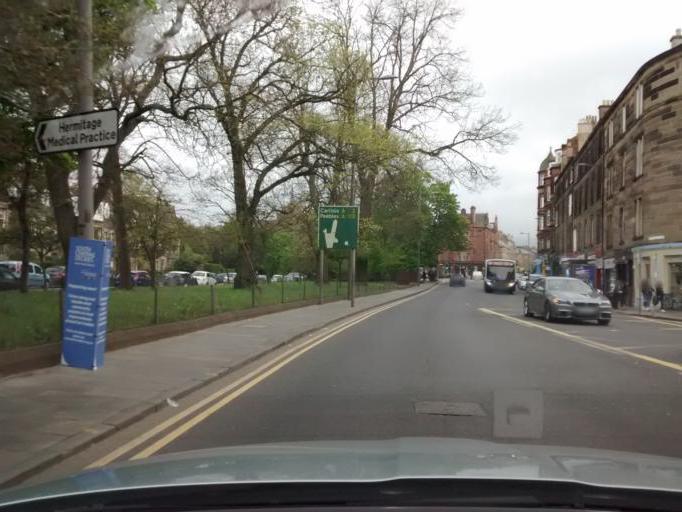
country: GB
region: Scotland
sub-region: Edinburgh
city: Edinburgh
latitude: 55.9264
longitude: -3.2091
